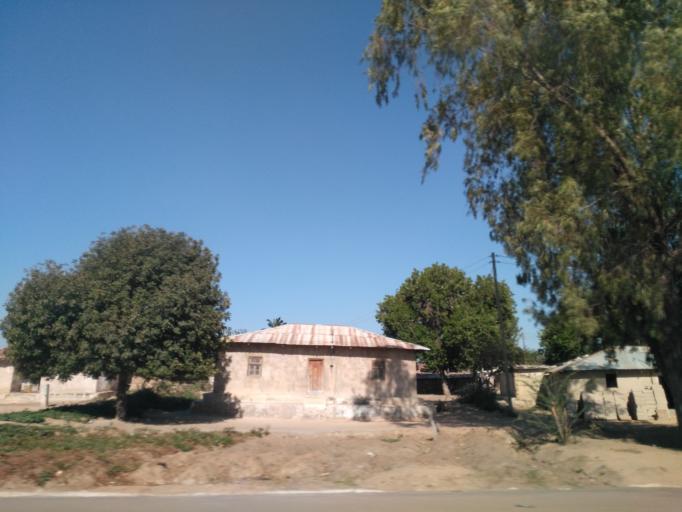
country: TZ
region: Dodoma
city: Dodoma
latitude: -6.1496
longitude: 35.7475
